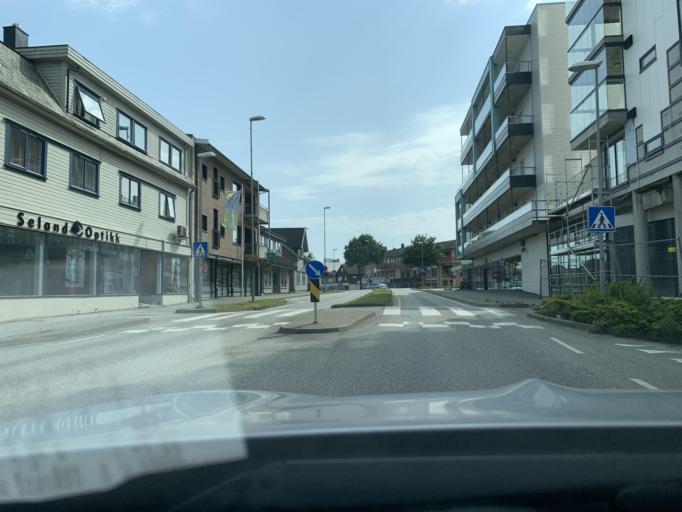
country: NO
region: Rogaland
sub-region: Klepp
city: Kleppe
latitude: 58.7752
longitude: 5.6295
